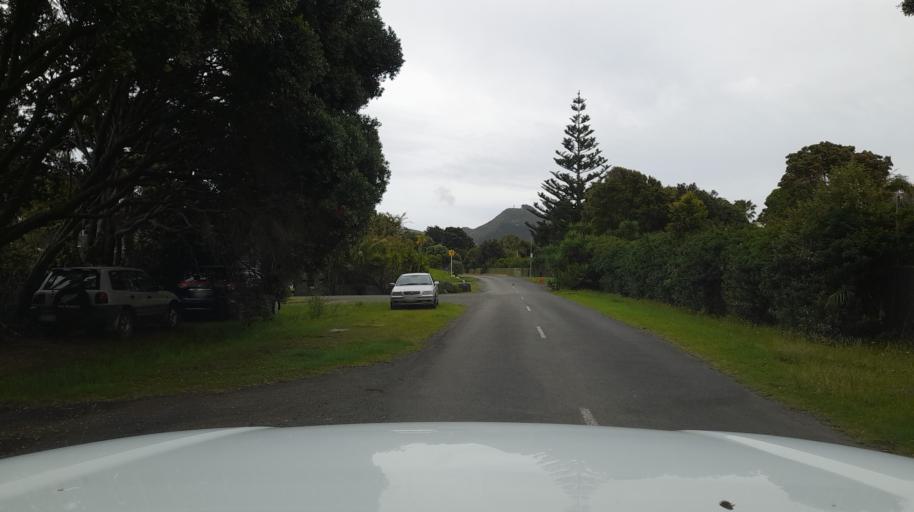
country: NZ
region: Northland
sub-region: Far North District
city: Ahipara
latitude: -35.1597
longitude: 173.1602
